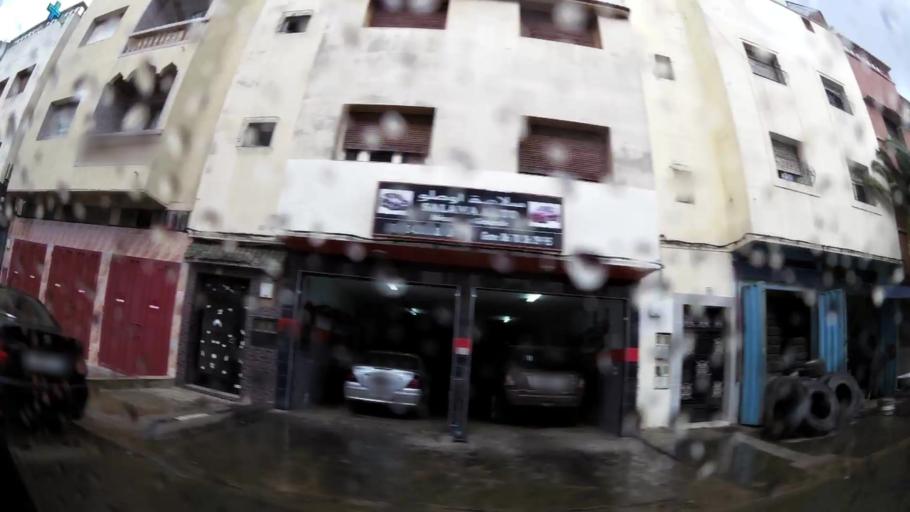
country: MA
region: Grand Casablanca
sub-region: Mohammedia
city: Mohammedia
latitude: 33.6746
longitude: -7.3963
